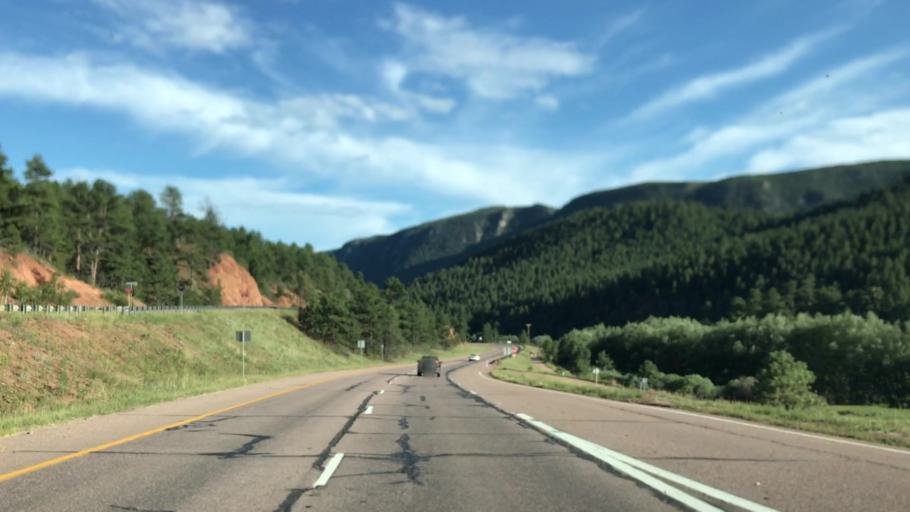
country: US
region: Colorado
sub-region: El Paso County
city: Cascade-Chipita Park
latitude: 38.9536
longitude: -105.0266
